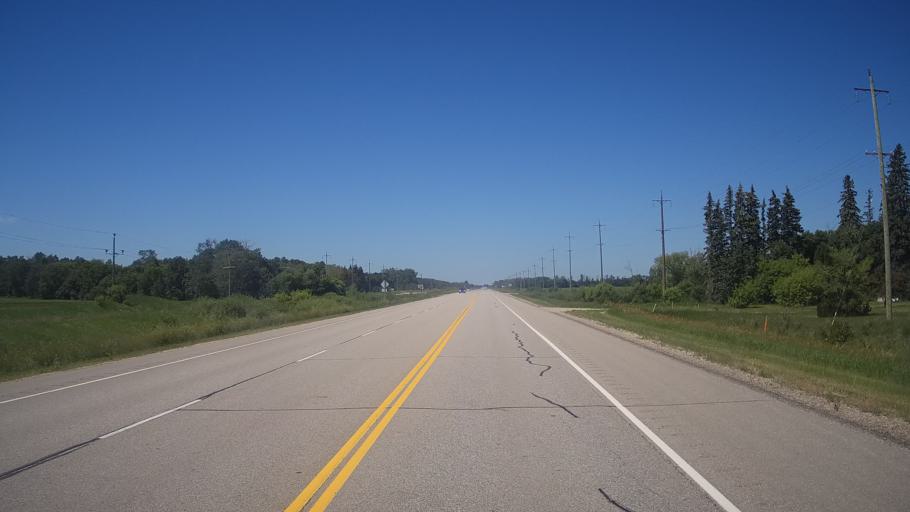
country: CA
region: Manitoba
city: Neepawa
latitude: 50.2253
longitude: -99.3364
